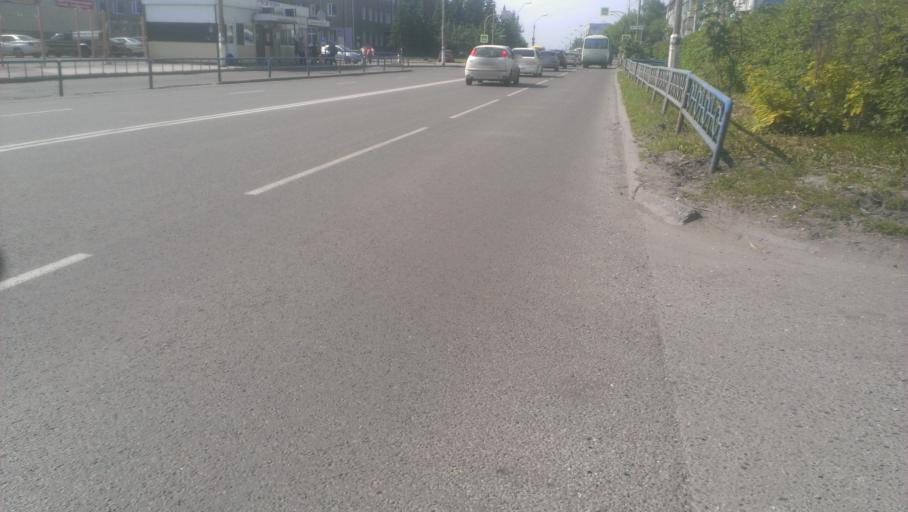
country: RU
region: Altai Krai
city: Novoaltaysk
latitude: 53.3925
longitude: 83.9342
